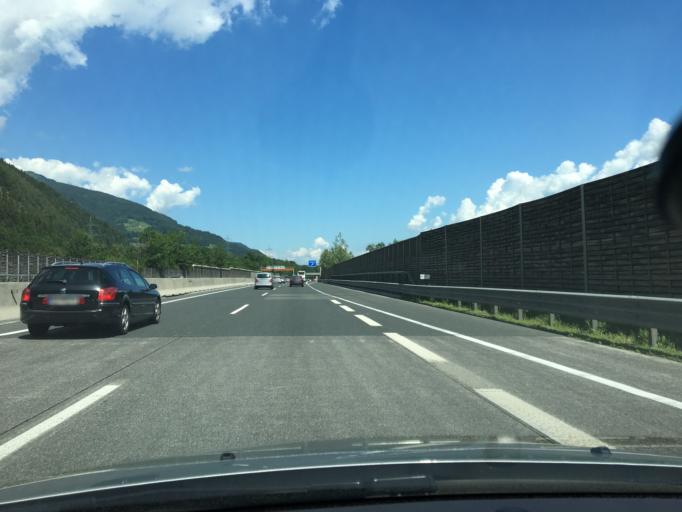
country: AT
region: Salzburg
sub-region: Politischer Bezirk Hallein
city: Golling an der Salzach
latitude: 47.5866
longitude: 13.1553
